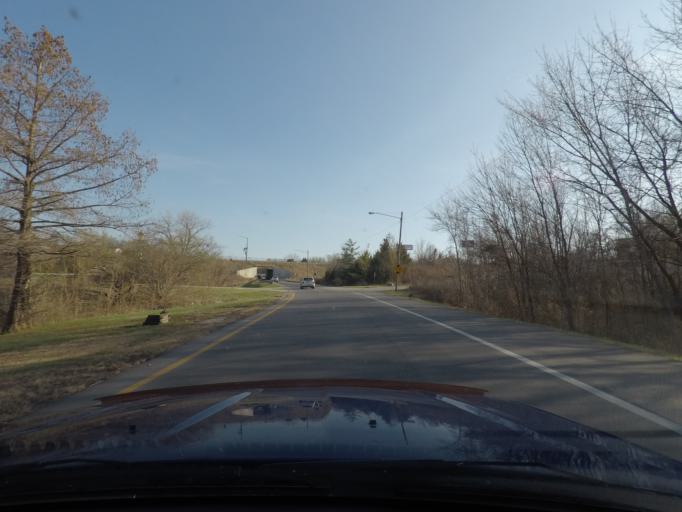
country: US
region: Kansas
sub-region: Douglas County
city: Lawrence
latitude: 38.9742
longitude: -95.2613
